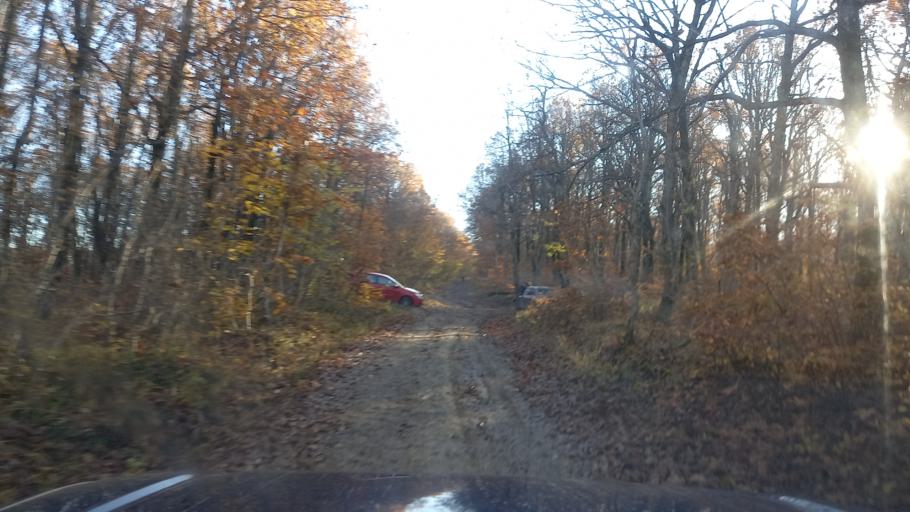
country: RU
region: Krasnodarskiy
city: Goryachiy Klyuch
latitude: 44.6171
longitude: 39.1044
